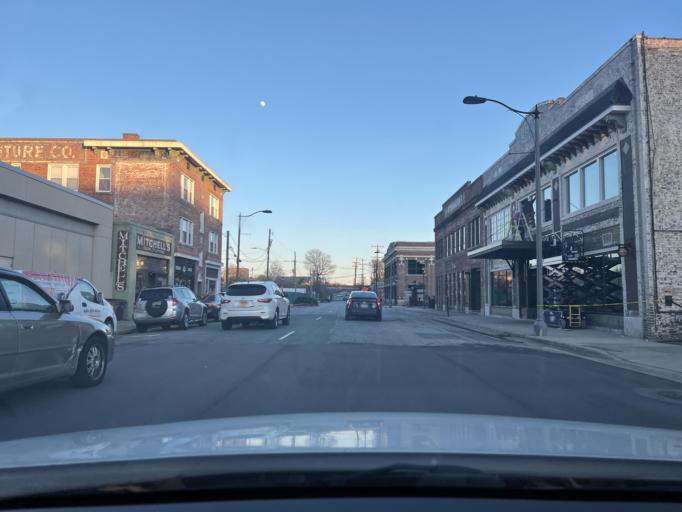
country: US
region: North Carolina
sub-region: Guilford County
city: Greensboro
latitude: 36.0723
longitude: -79.7867
